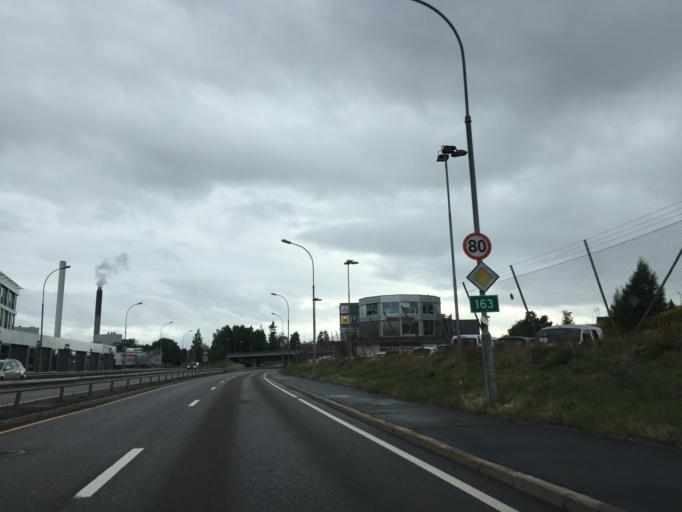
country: NO
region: Oslo
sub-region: Oslo
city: Oslo
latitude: 59.9350
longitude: 10.8315
